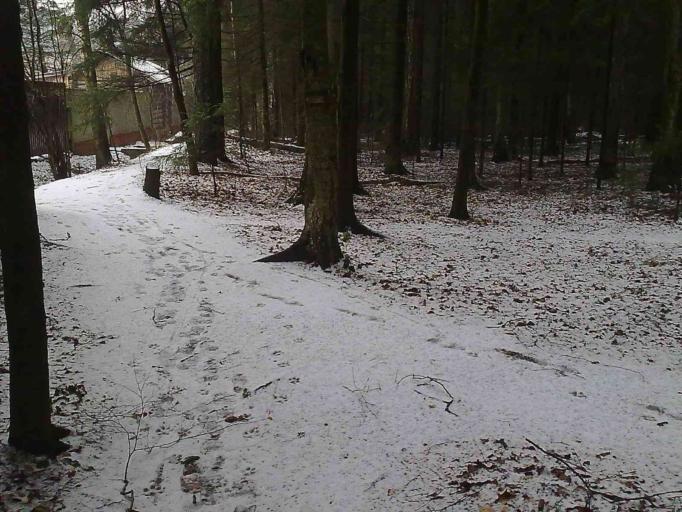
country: RU
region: Moskovskaya
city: Lesnoy Gorodok
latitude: 55.6647
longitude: 37.1572
